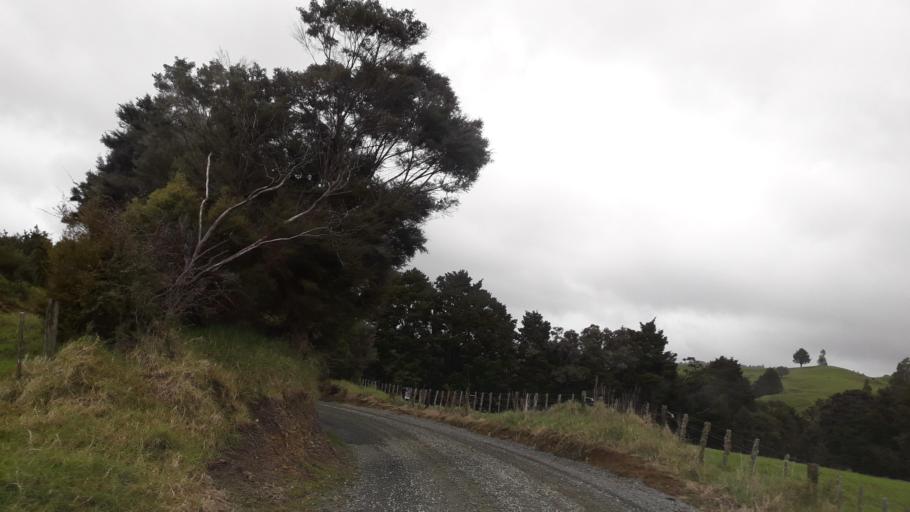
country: NZ
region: Northland
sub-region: Far North District
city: Waimate North
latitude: -35.1505
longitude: 173.7119
